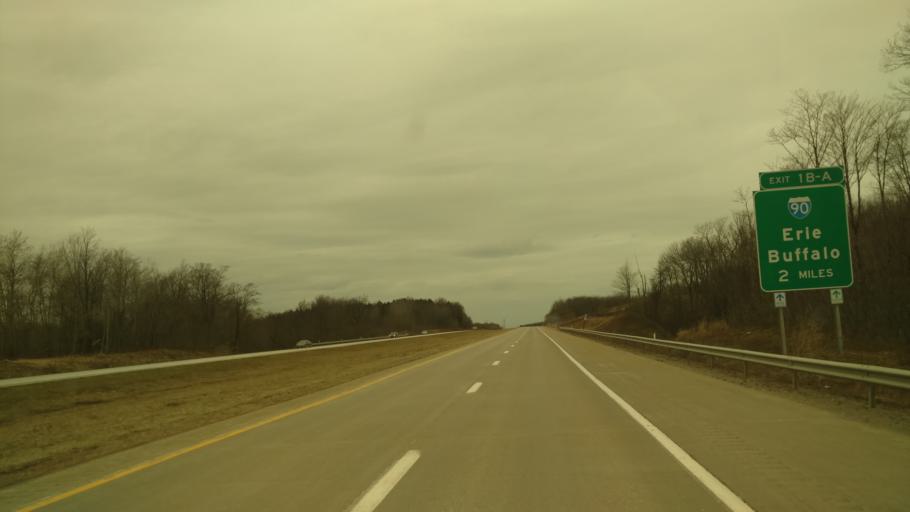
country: US
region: Pennsylvania
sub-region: Erie County
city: North East
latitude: 42.1476
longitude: -79.8469
